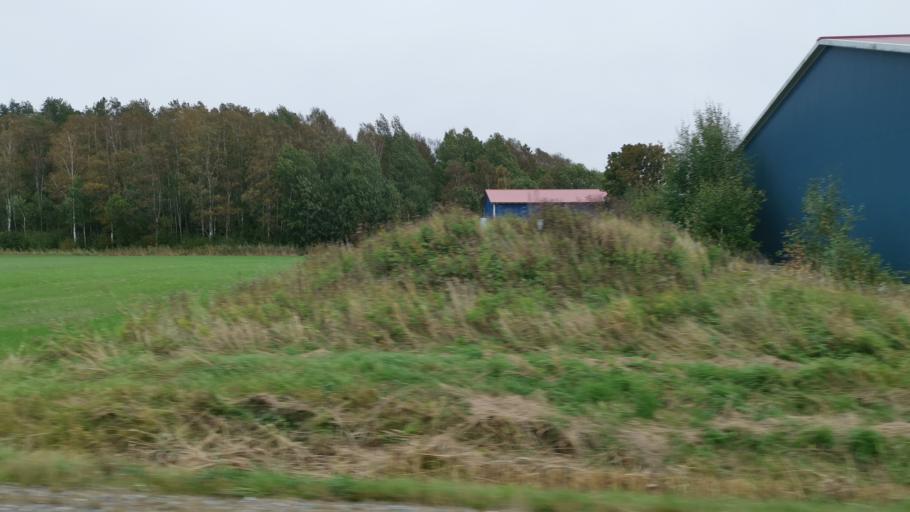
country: SE
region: Vaestra Goetaland
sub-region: Tanums Kommun
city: Tanumshede
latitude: 58.6629
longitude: 11.3461
